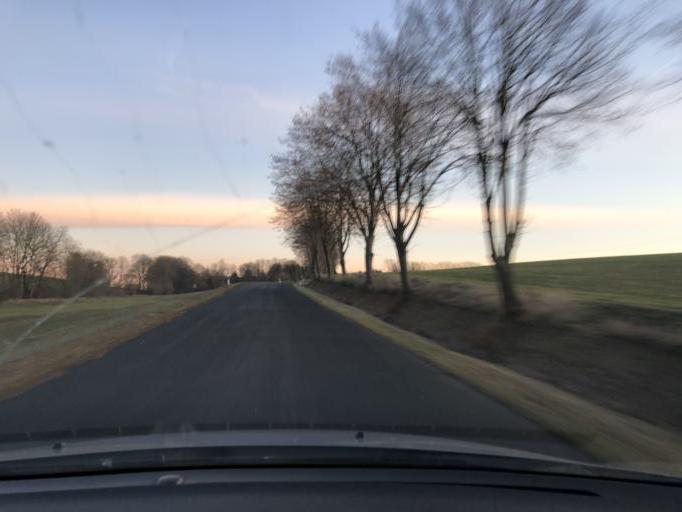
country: DE
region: Thuringia
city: Blankenhain
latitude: 50.8445
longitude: 11.3638
